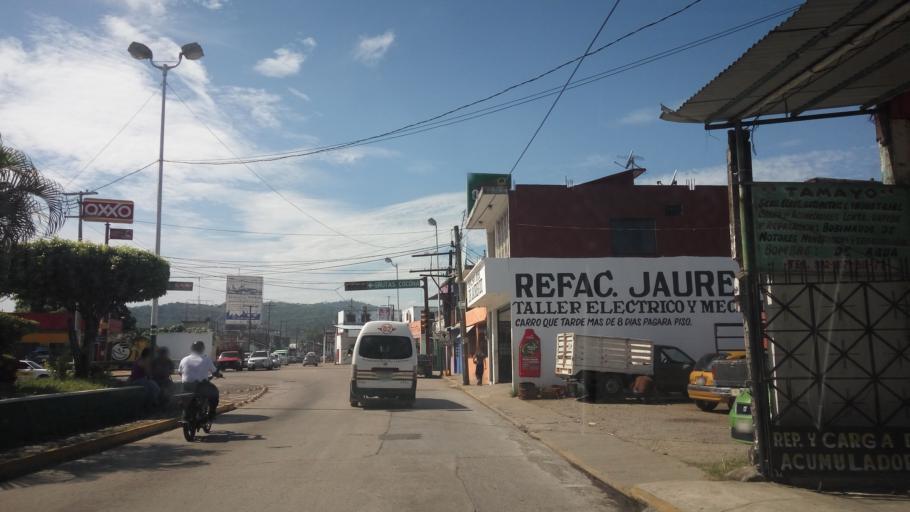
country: MX
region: Tabasco
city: Teapa
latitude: 17.5615
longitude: -92.9504
